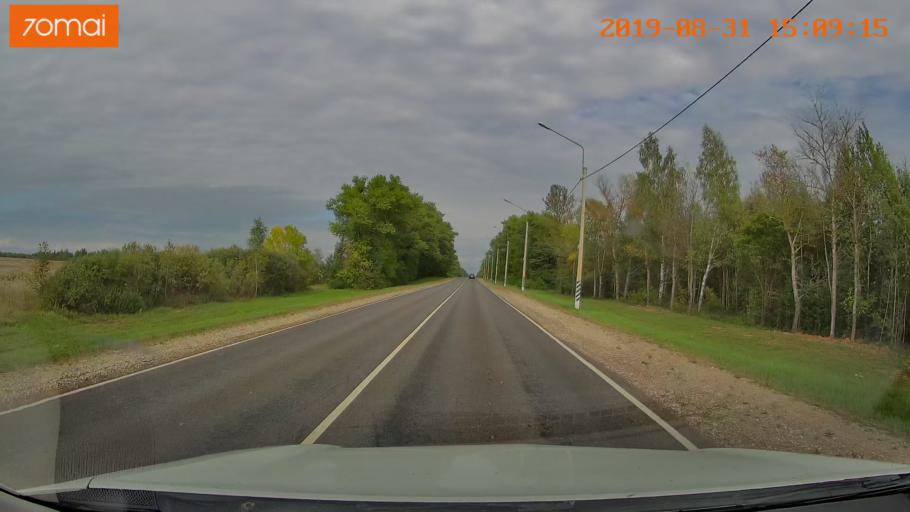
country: RU
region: Kaluga
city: Spas-Demensk
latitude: 54.3997
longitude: 34.1972
